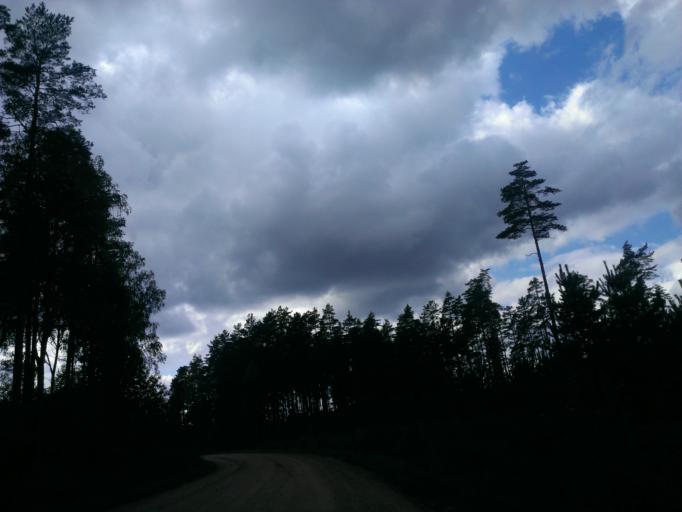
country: LV
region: Incukalns
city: Vangazi
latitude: 57.0612
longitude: 24.6101
